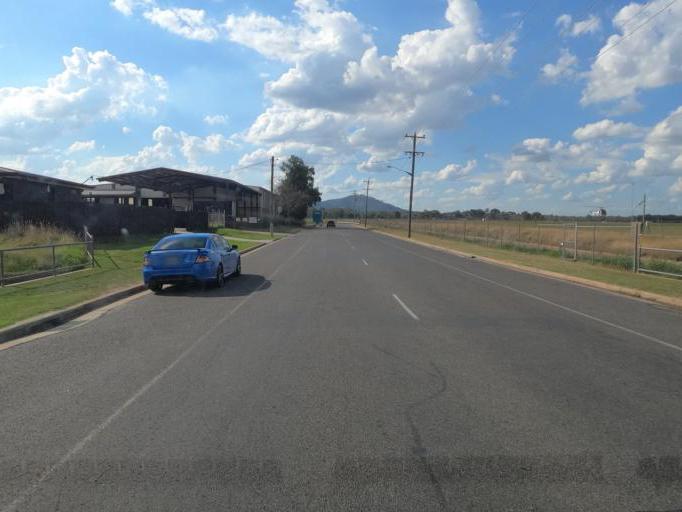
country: AU
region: New South Wales
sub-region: Albury Municipality
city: East Albury
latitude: -36.0727
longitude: 146.9481
